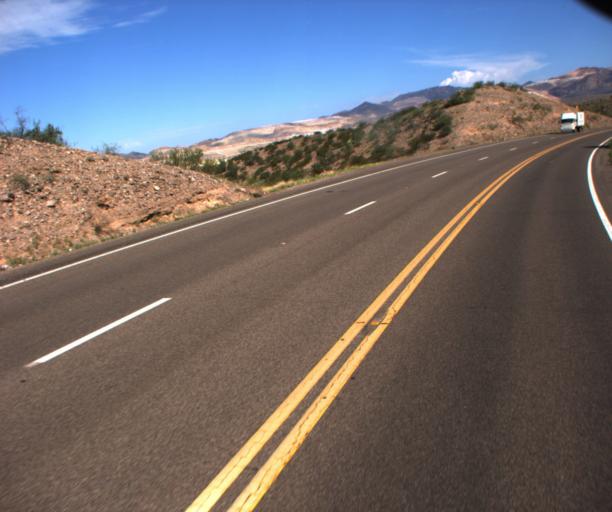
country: US
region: Arizona
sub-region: Greenlee County
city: Clifton
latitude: 33.0157
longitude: -109.2866
